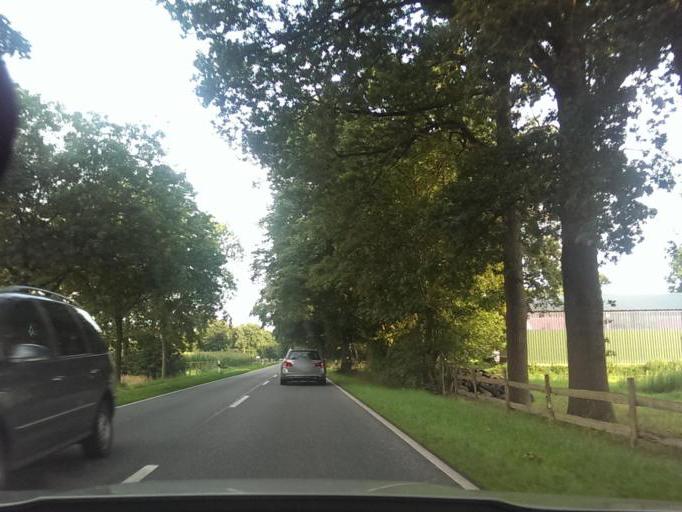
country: DE
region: Lower Saxony
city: Lilienthal
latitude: 53.1802
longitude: 8.8782
